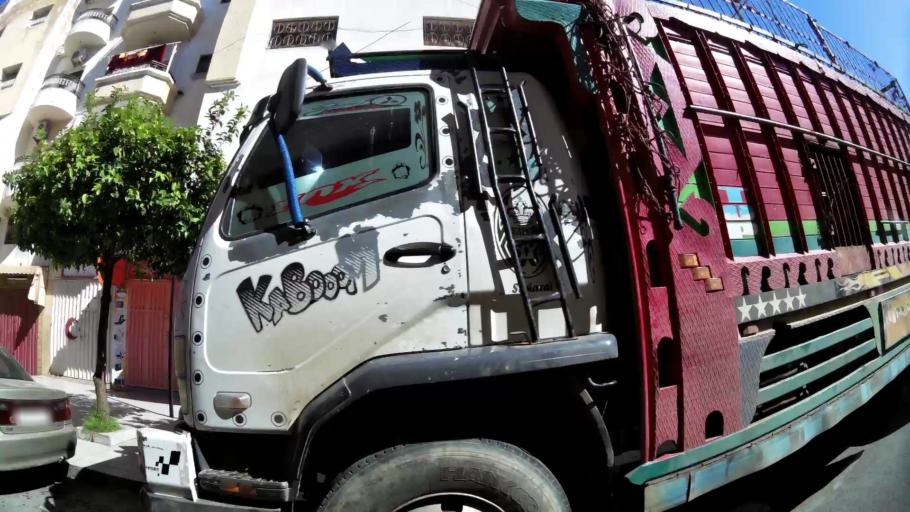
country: MA
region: Fes-Boulemane
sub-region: Fes
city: Fes
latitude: 34.0123
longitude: -4.9798
